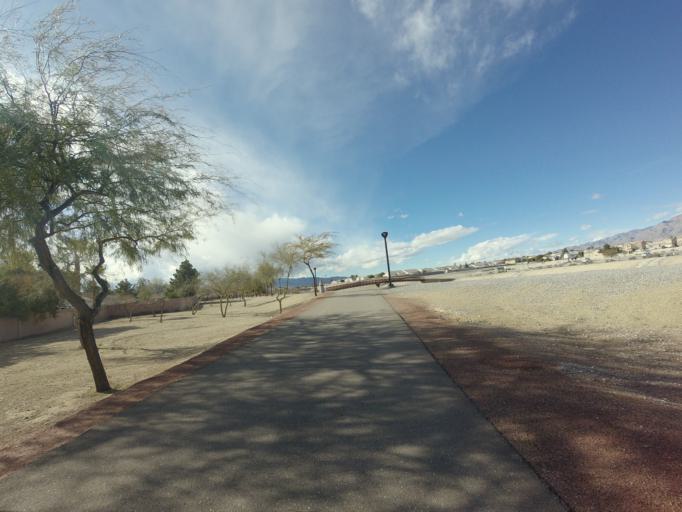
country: US
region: Nevada
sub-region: Clark County
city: North Las Vegas
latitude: 36.2553
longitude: -115.1643
